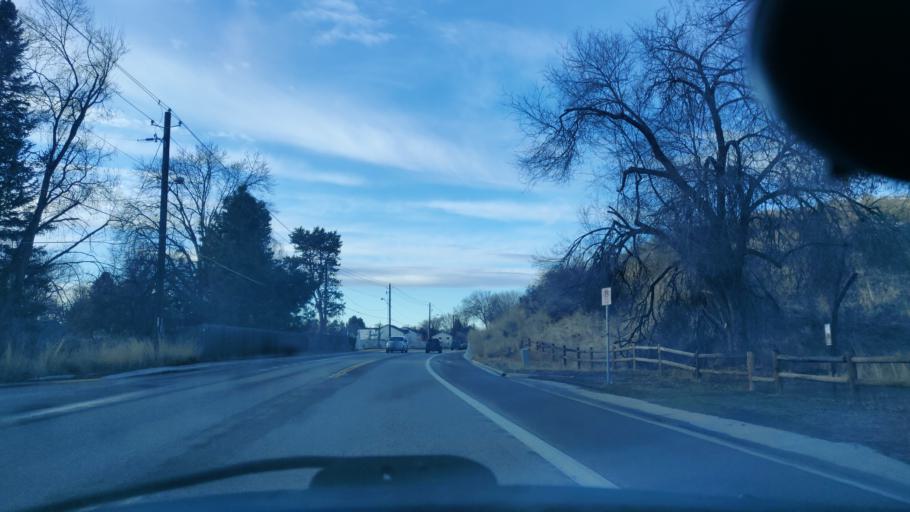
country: US
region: Idaho
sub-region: Ada County
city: Garden City
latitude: 43.6516
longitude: -116.2273
